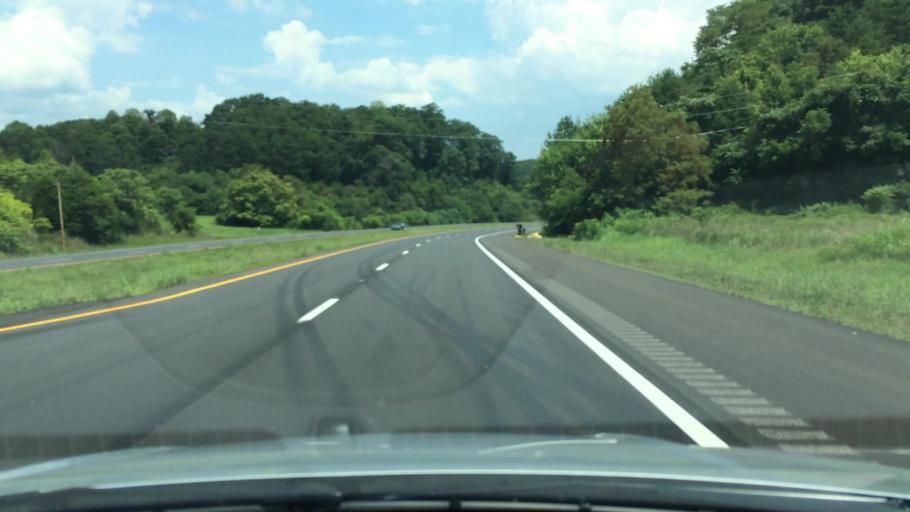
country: US
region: Tennessee
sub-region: Hamblen County
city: Morristown
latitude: 36.1888
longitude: -83.2616
